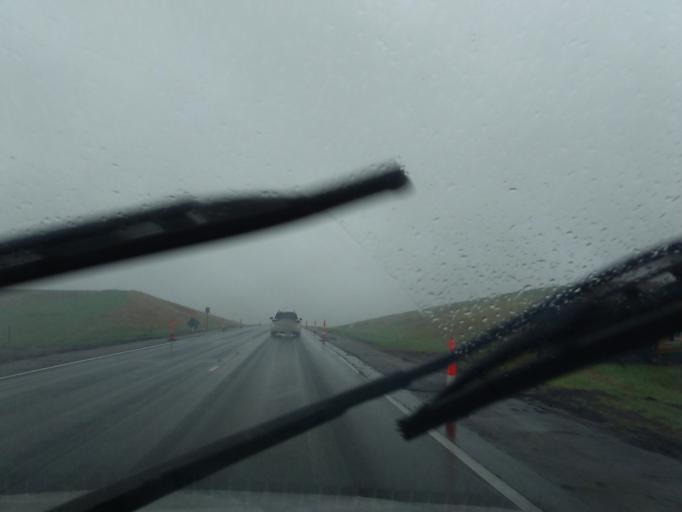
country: US
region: Nebraska
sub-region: Wayne County
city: Wayne
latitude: 42.1707
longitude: -97.1901
